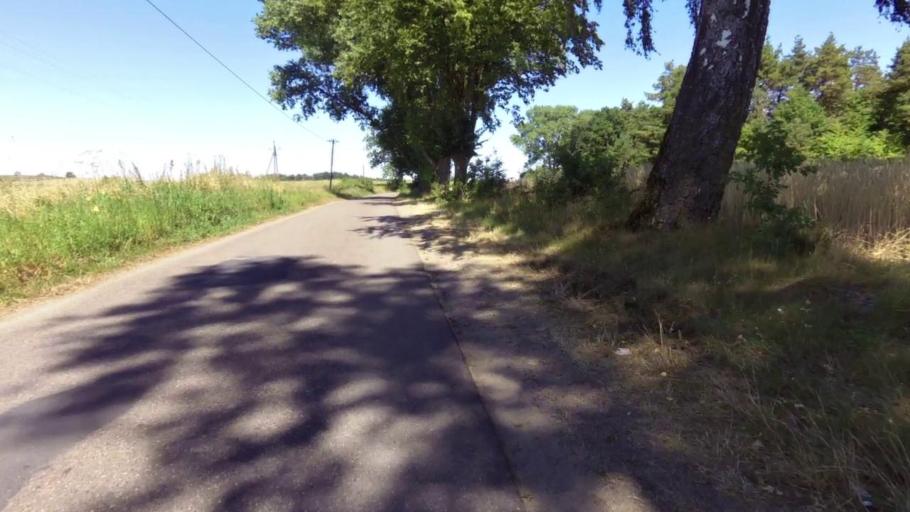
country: PL
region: West Pomeranian Voivodeship
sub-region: Powiat drawski
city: Czaplinek
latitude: 53.5402
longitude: 16.2089
